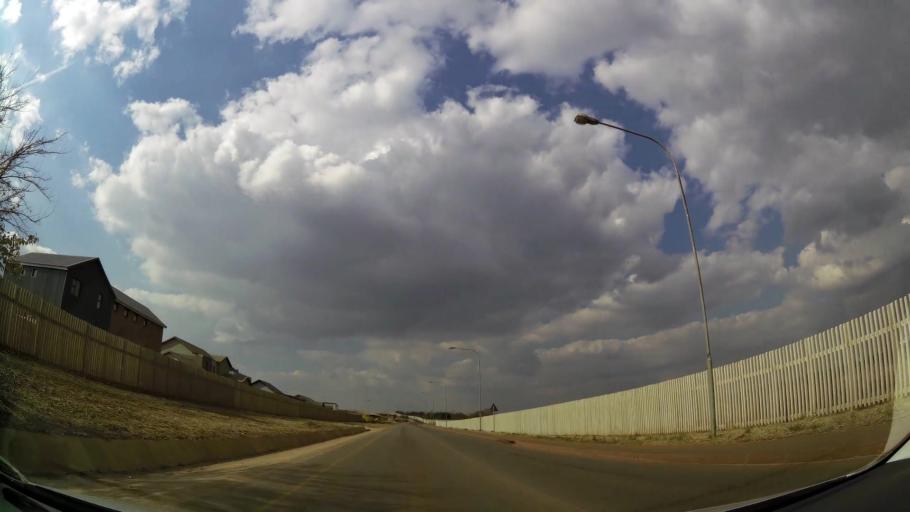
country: ZA
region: Gauteng
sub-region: Ekurhuleni Metropolitan Municipality
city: Tembisa
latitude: -25.9302
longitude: 28.2113
